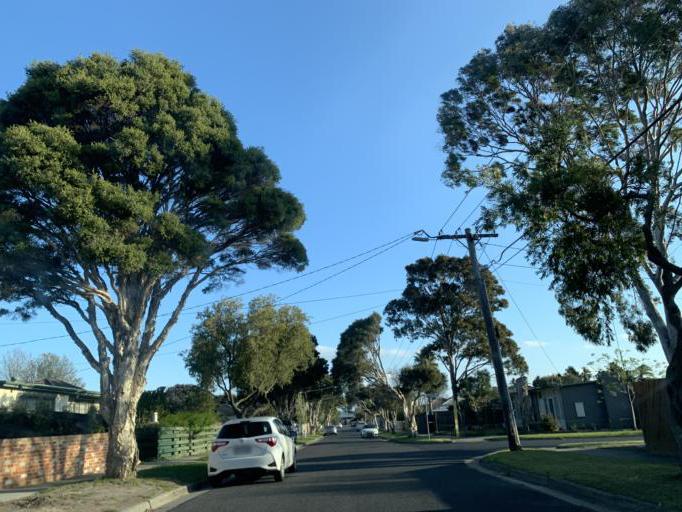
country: AU
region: Victoria
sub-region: Kingston
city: Mordialloc
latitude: -37.9864
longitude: 145.0959
